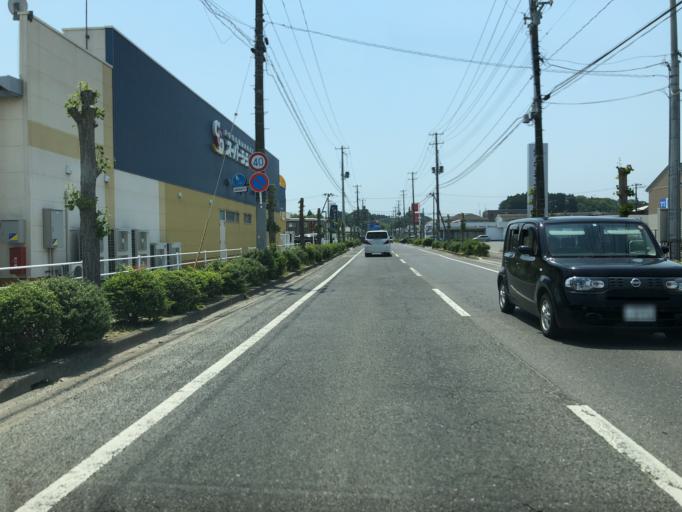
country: JP
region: Miyagi
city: Marumori
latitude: 37.8049
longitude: 140.9126
